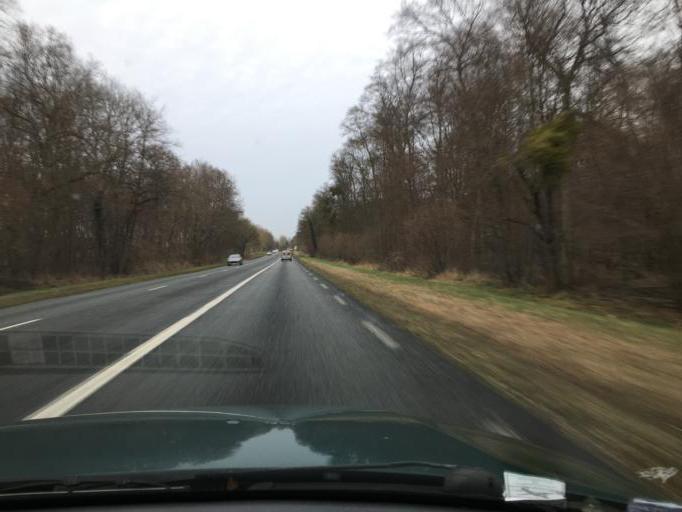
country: FR
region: Picardie
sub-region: Departement de l'Oise
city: Senlis
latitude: 49.1860
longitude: 2.5704
